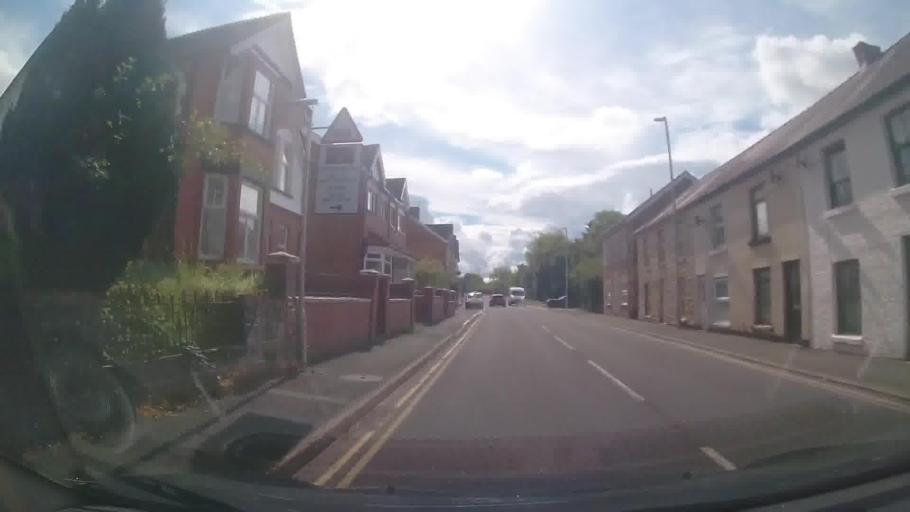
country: GB
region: Wales
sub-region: Sir Powys
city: Llandrindod Wells
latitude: 52.2492
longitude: -3.3754
